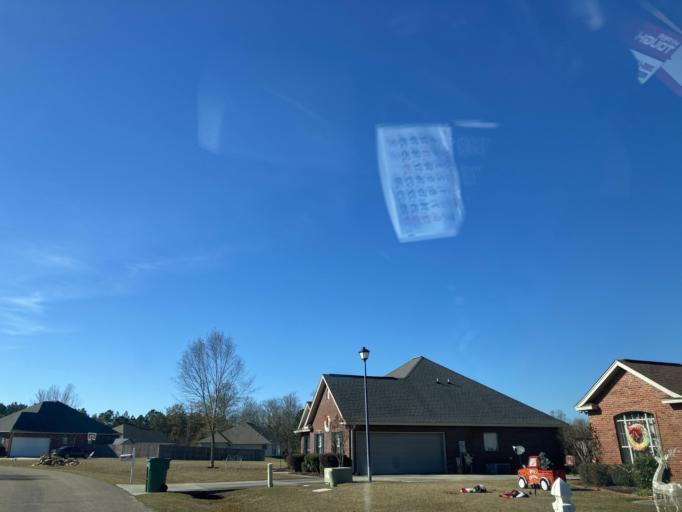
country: US
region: Mississippi
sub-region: Forrest County
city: Petal
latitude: 31.3229
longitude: -89.1854
